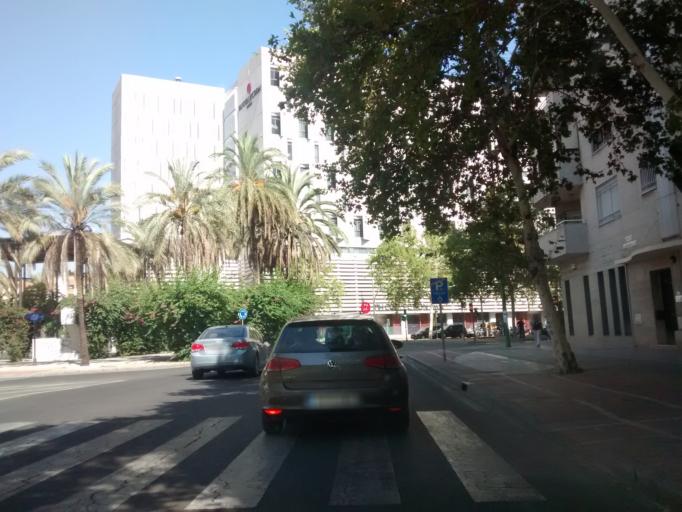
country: ES
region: Andalusia
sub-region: Provincia de Sevilla
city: Sevilla
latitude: 37.3745
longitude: -5.9753
